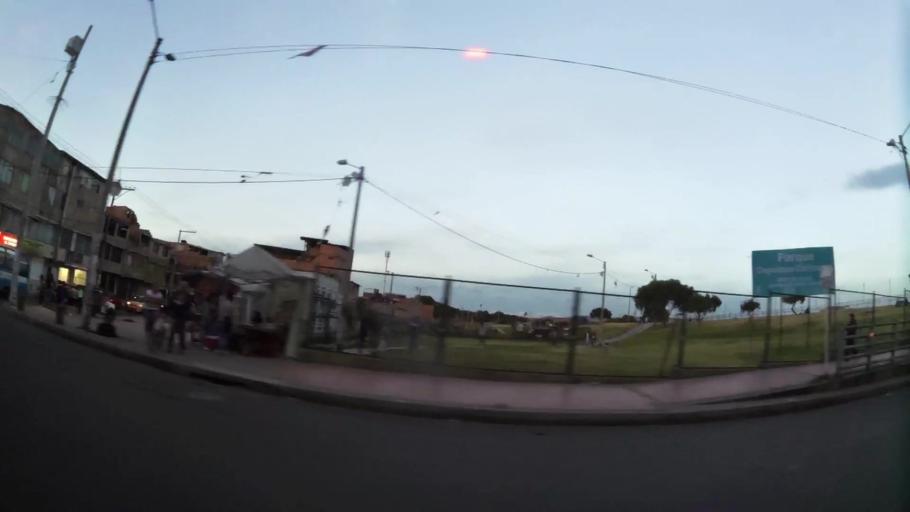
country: CO
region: Cundinamarca
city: Soacha
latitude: 4.6236
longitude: -74.1640
